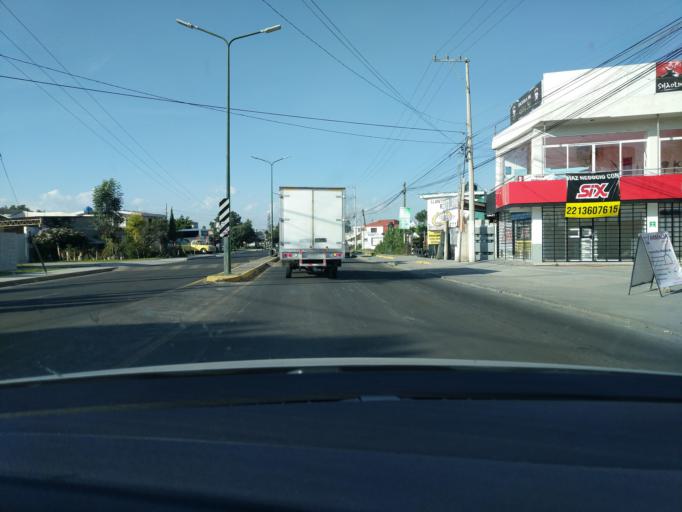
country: MX
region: Puebla
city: San Andres Cholula
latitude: 19.0400
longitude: -98.3156
